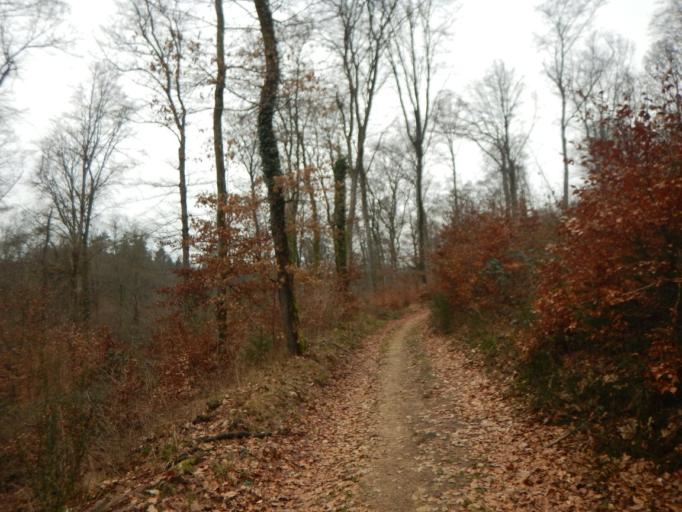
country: LU
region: Luxembourg
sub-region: Canton de Capellen
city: Koerich
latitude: 49.6782
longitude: 5.9556
